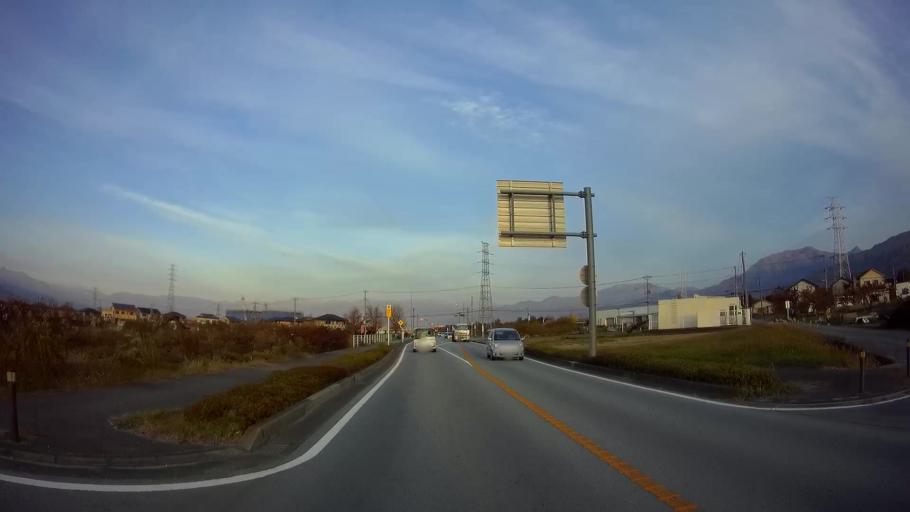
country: JP
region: Yamanashi
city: Isawa
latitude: 35.6079
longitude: 138.6109
